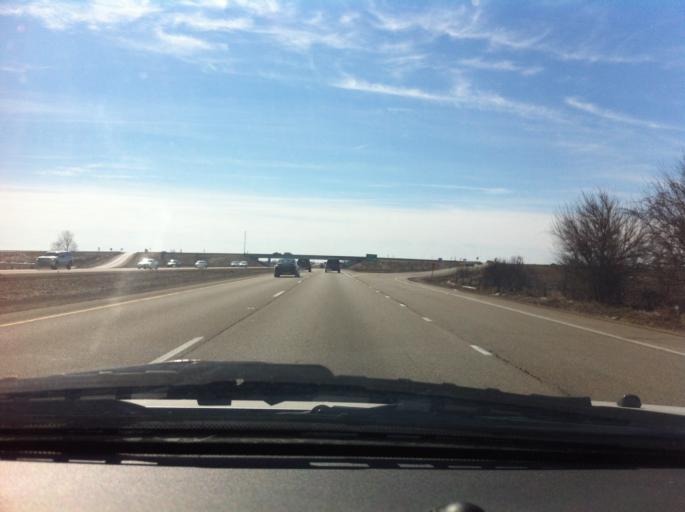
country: US
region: Wisconsin
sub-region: Rock County
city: Janesville
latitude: 42.6908
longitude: -88.9841
